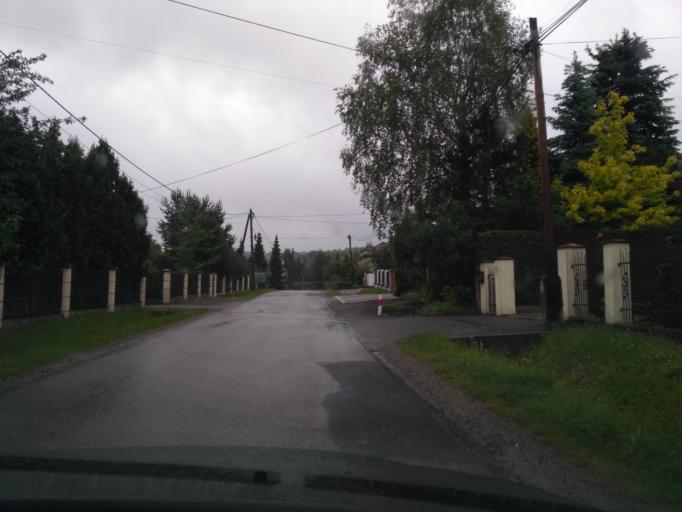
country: PL
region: Lesser Poland Voivodeship
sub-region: Powiat gorlicki
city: Gorlice
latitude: 49.6678
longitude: 21.1411
